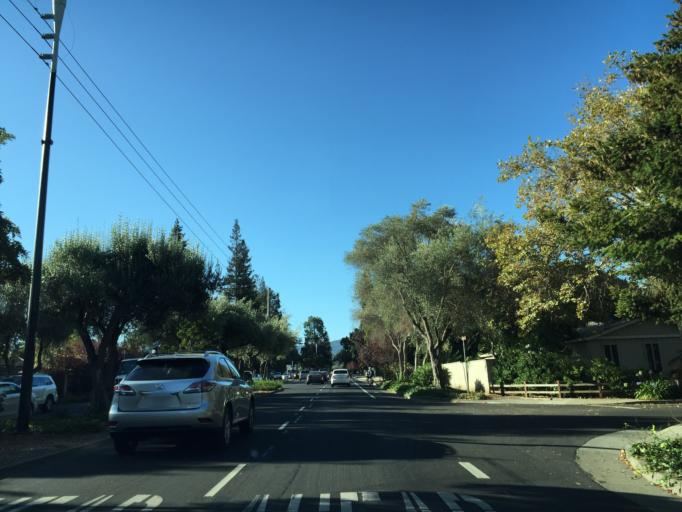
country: US
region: California
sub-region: Santa Clara County
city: Los Altos
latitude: 37.3861
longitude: -122.1143
